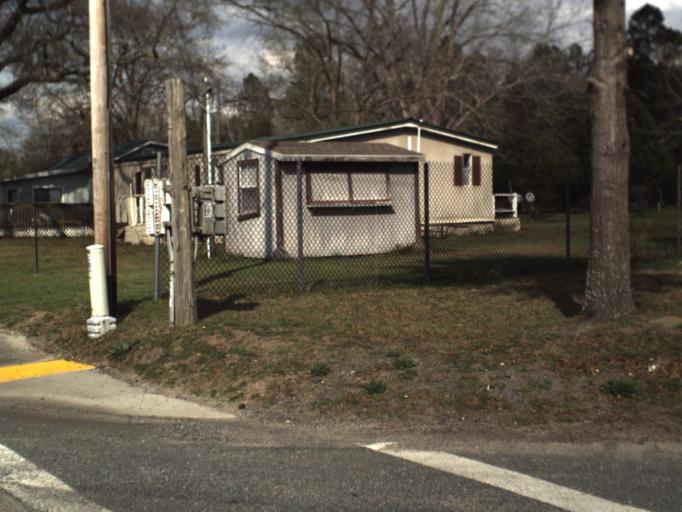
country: US
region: Florida
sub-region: Bay County
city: Youngstown
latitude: 30.3764
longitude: -85.4382
